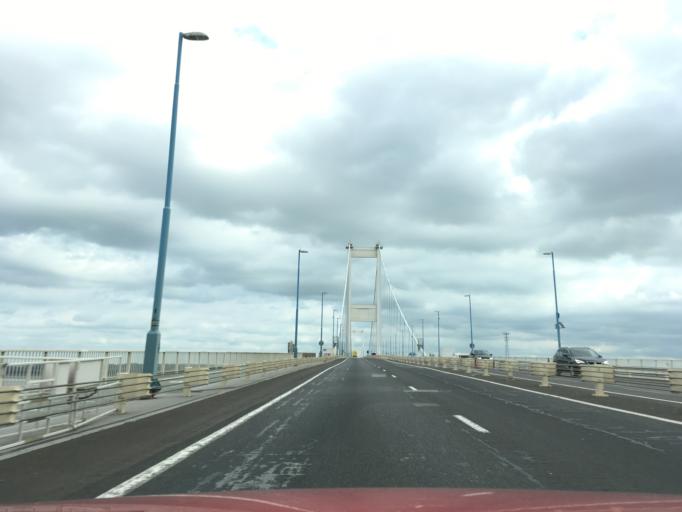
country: GB
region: Wales
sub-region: Monmouthshire
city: Chepstow
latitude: 51.6145
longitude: -2.6519
